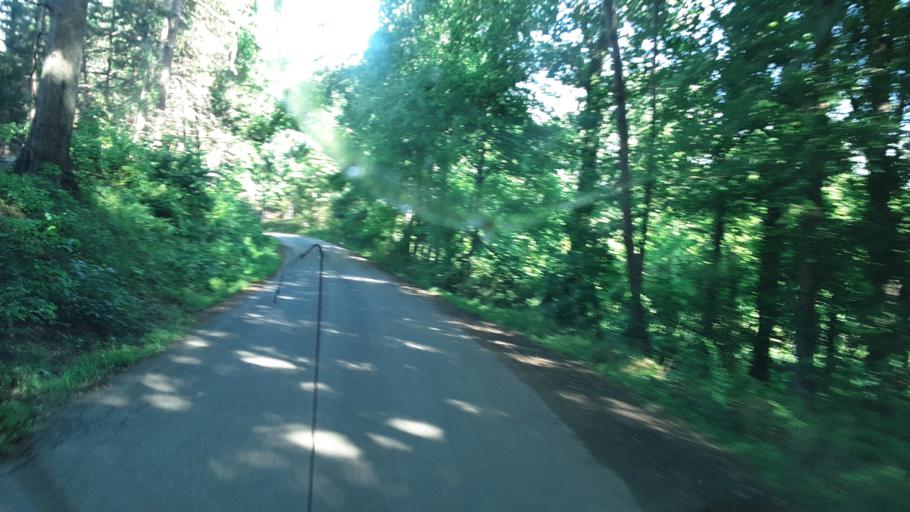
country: US
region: Virginia
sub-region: Pittsylvania County
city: Chatham
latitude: 36.8391
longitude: -79.4074
